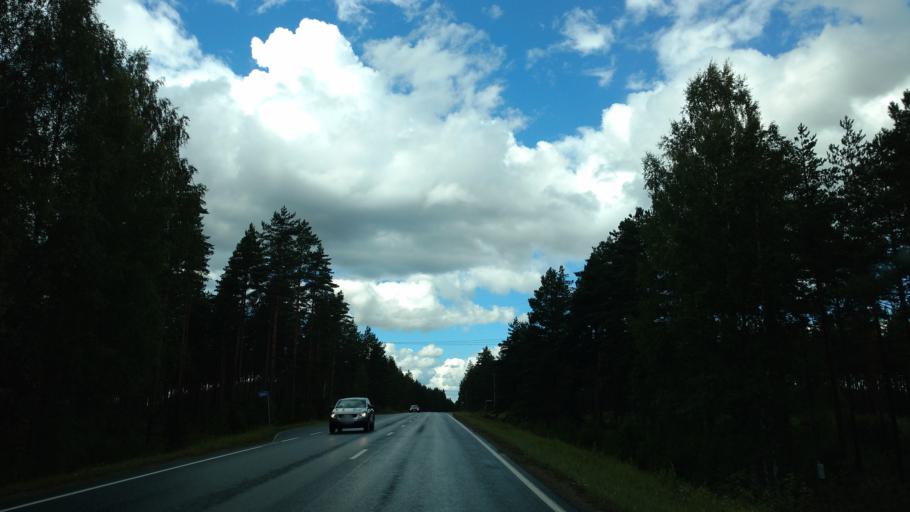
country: FI
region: Varsinais-Suomi
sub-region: Salo
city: Muurla
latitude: 60.2934
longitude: 23.3376
